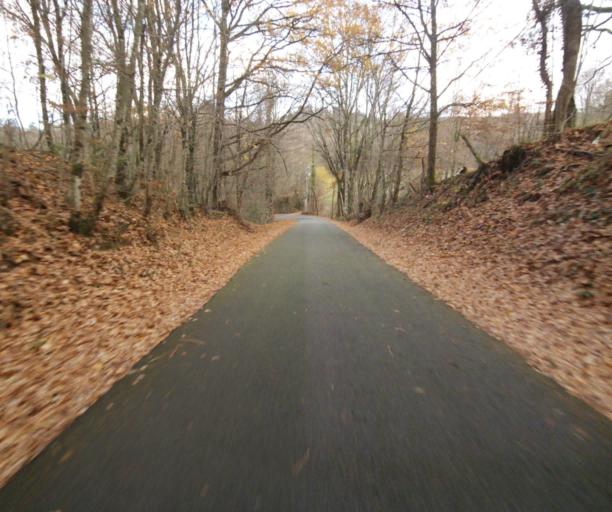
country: FR
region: Limousin
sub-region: Departement de la Correze
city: Sainte-Fortunade
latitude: 45.2102
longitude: 1.7823
